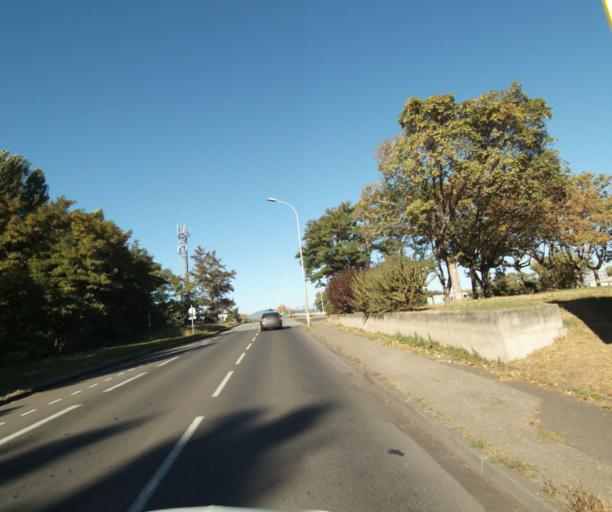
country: FR
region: Auvergne
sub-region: Departement du Puy-de-Dome
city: Gerzat
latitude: 45.8224
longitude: 3.1395
